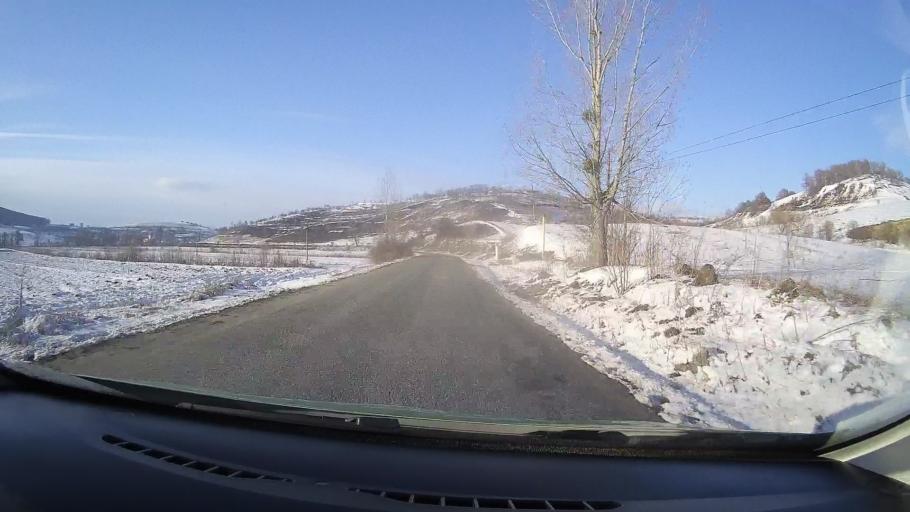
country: RO
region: Sibiu
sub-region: Comuna Merghindeal
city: Merghindeal
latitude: 45.9734
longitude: 24.7072
